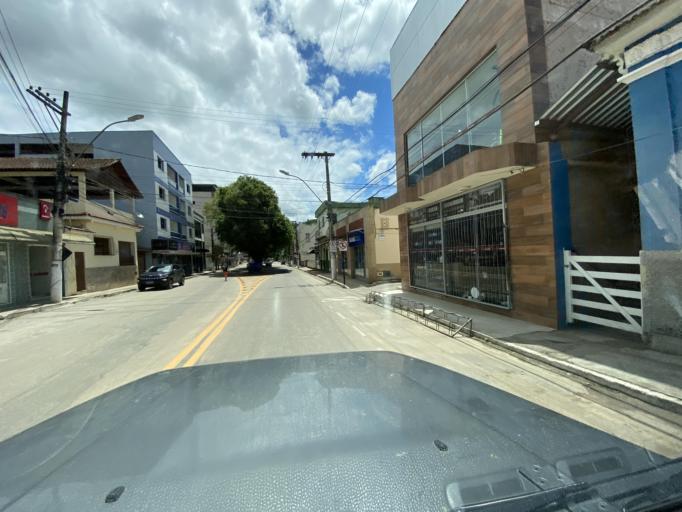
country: BR
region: Espirito Santo
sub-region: Jeronimo Monteiro
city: Jeronimo Monteiro
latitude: -20.7882
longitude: -41.3932
